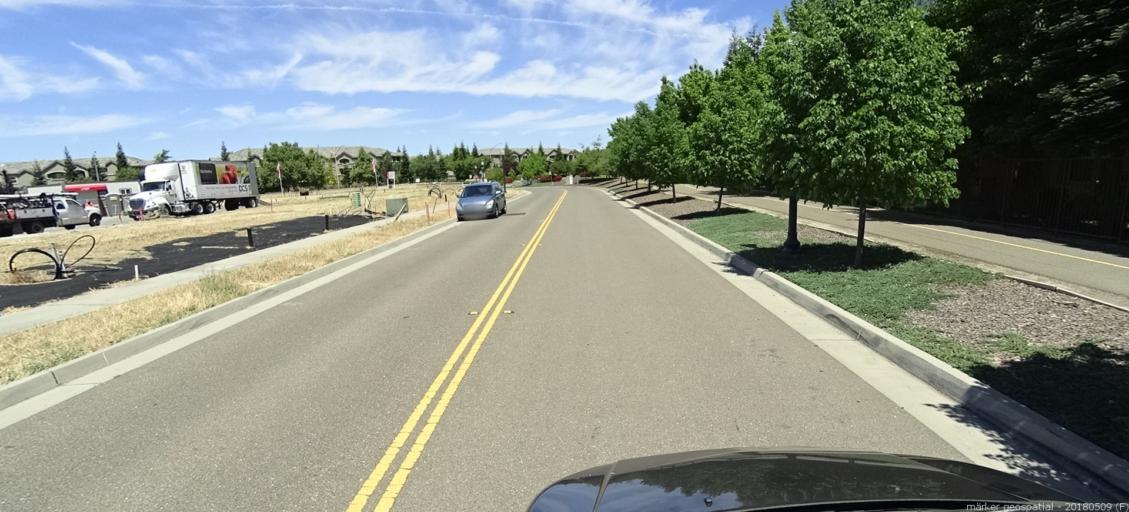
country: US
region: California
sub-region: Yolo County
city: West Sacramento
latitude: 38.6434
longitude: -121.5143
